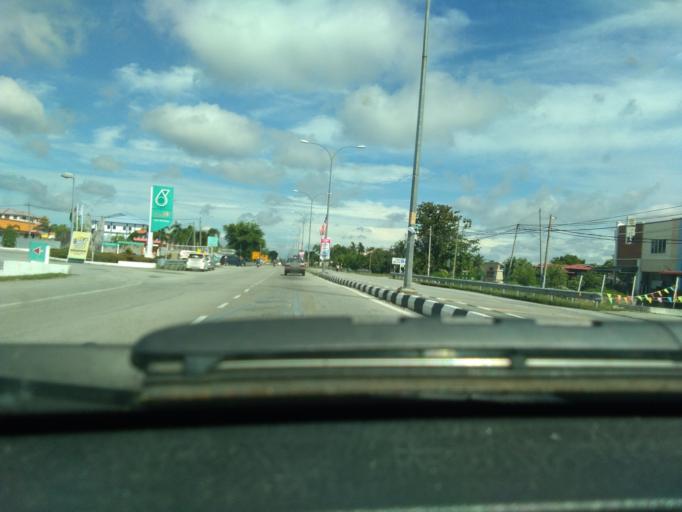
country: MY
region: Perak
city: Bagan Serai
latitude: 5.0044
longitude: 100.5463
